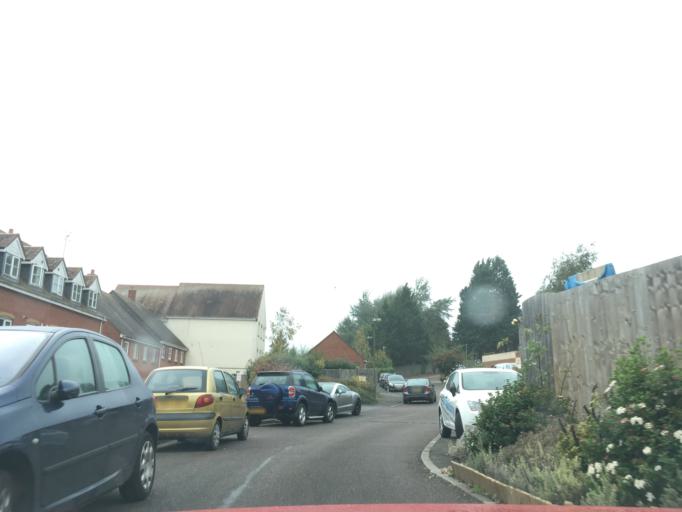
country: GB
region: England
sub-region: Gloucestershire
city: Stonehouse
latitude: 51.7420
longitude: -2.2419
